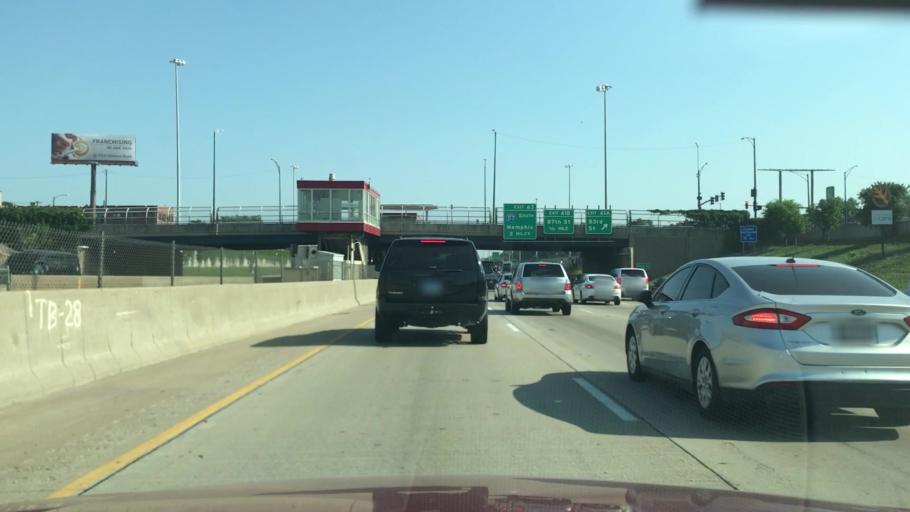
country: US
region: Illinois
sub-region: Cook County
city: Evergreen Park
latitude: 41.7519
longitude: -87.6254
